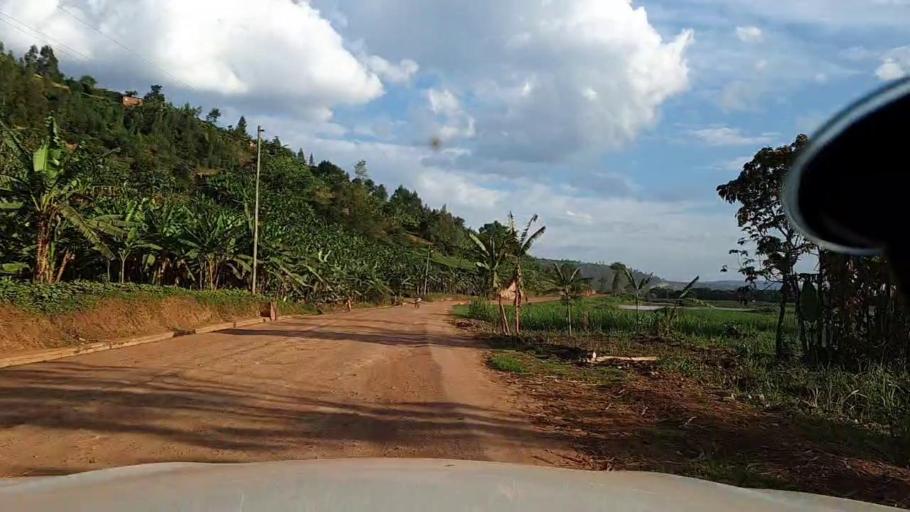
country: RW
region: Kigali
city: Kigali
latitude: -1.9333
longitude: 29.9967
